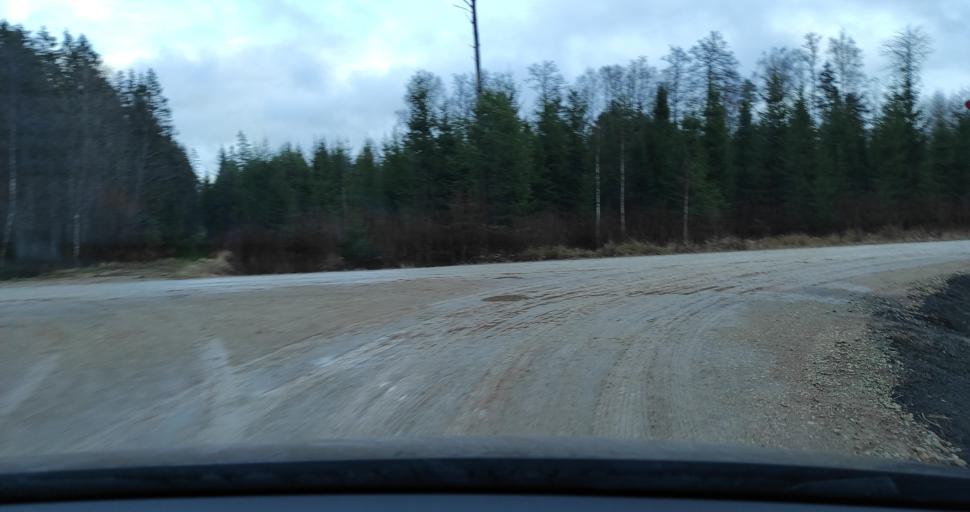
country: LV
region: Skrunda
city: Skrunda
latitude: 56.7426
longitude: 22.2053
